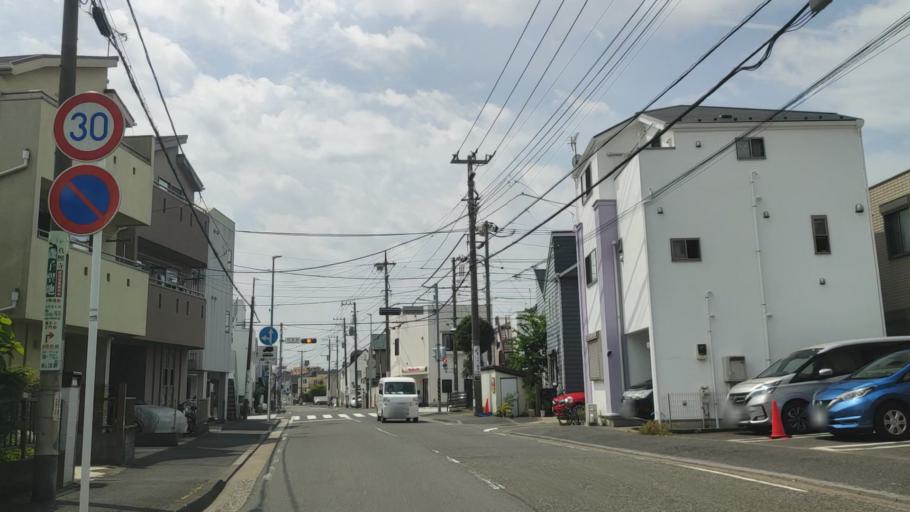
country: JP
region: Kanagawa
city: Yokohama
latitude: 35.4172
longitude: 139.6236
